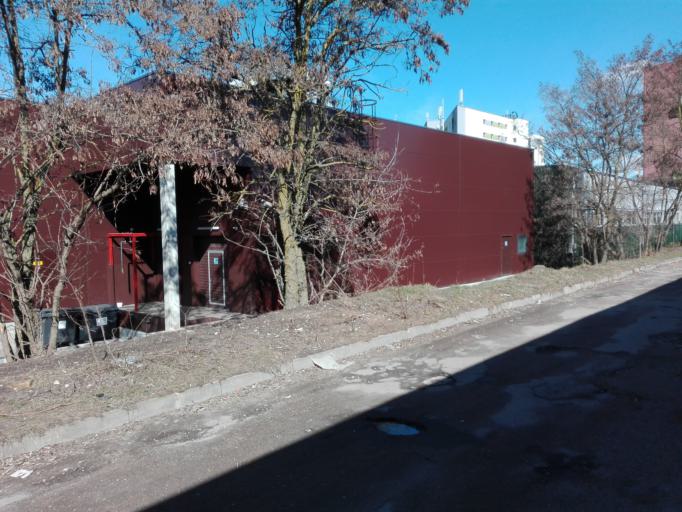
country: LT
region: Vilnius County
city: Justiniskes
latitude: 54.6975
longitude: 25.2117
